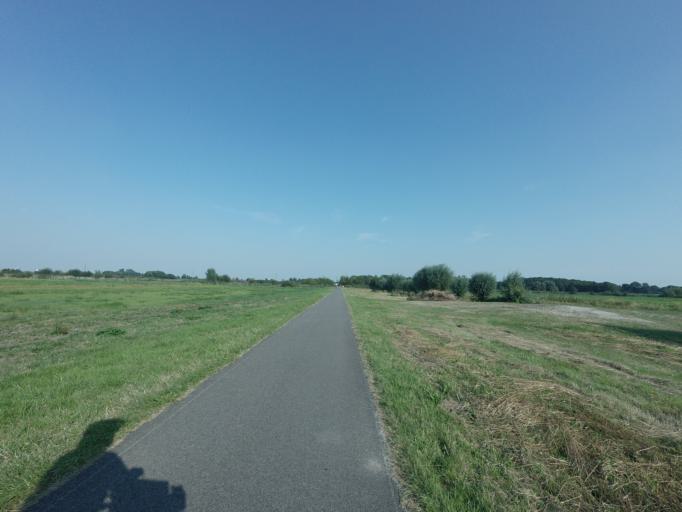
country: NL
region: Groningen
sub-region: Gemeente Zuidhorn
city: Aduard
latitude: 53.1692
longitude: 6.4848
